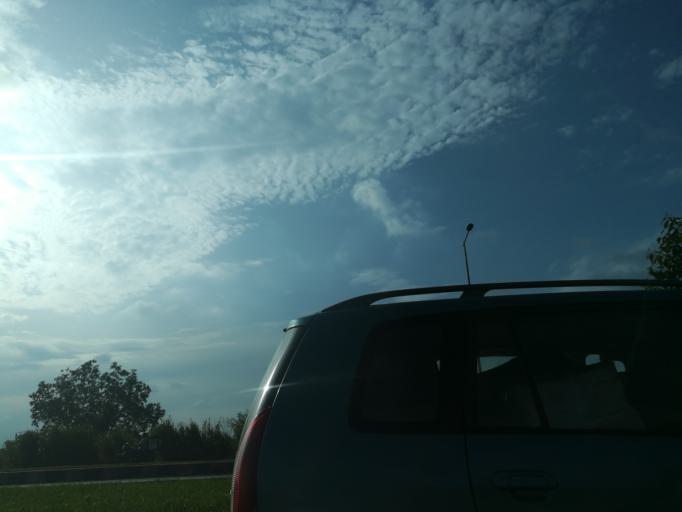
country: NG
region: Lagos
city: Ebute Ikorodu
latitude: 6.6183
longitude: 3.4484
